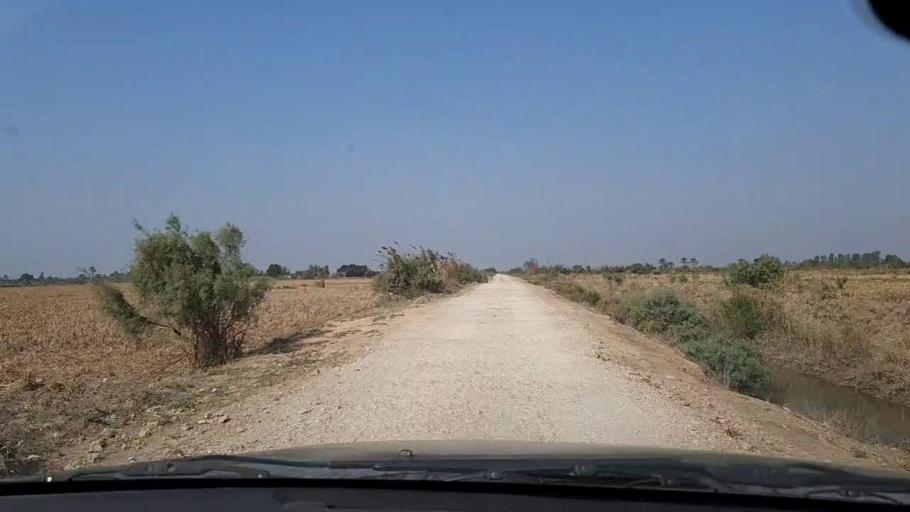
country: PK
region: Sindh
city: Mirpur Sakro
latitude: 24.3717
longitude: 67.6830
